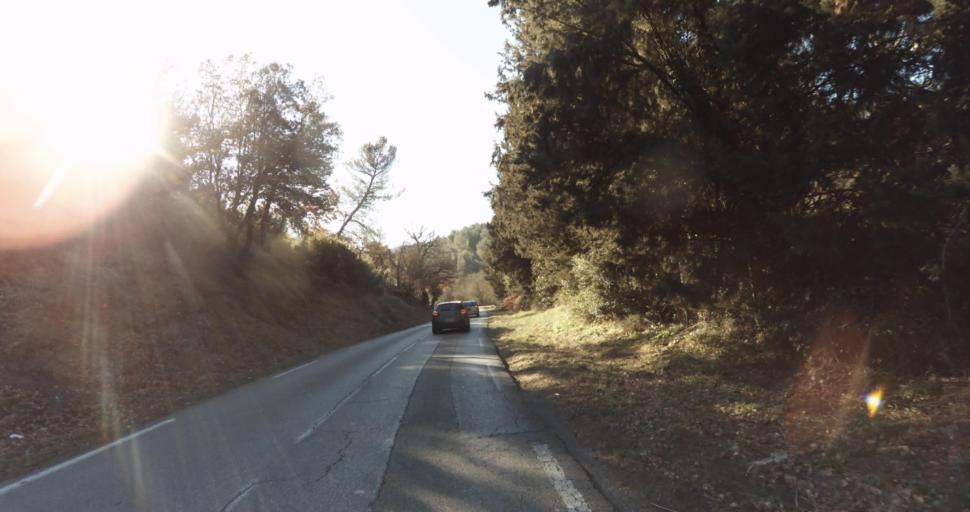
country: FR
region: Provence-Alpes-Cote d'Azur
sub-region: Departement des Bouches-du-Rhone
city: Cadolive
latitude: 43.4053
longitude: 5.5571
